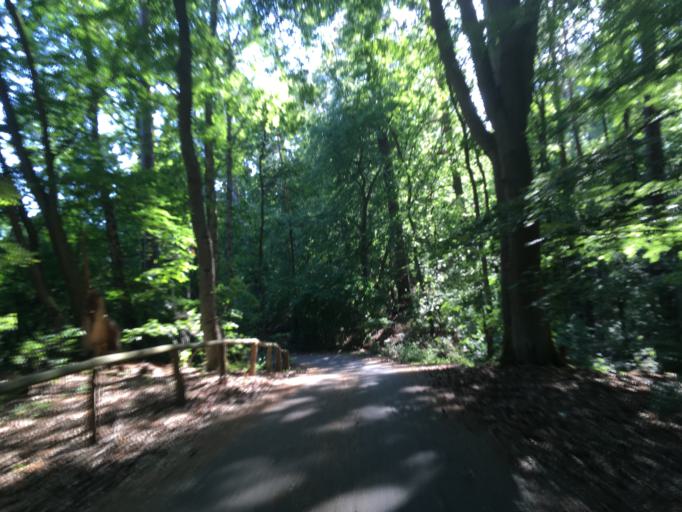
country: DE
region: Brandenburg
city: Joachimsthal
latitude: 52.9380
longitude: 13.7147
